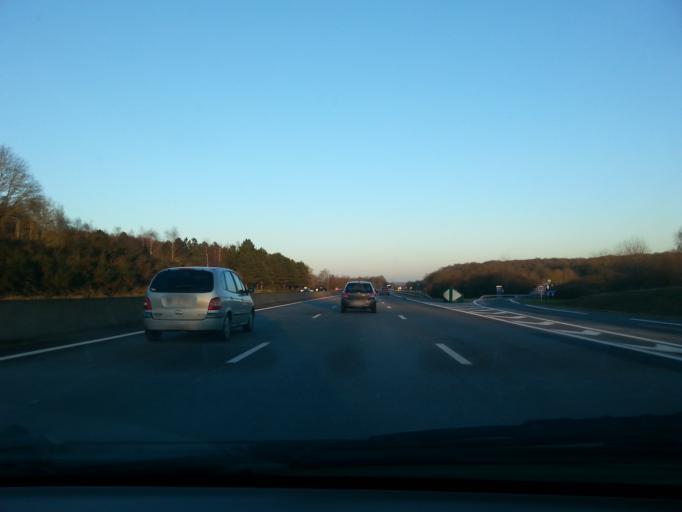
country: FR
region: Centre
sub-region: Departement d'Eure-et-Loir
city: Authon-du-Perche
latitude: 48.2119
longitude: 0.9370
